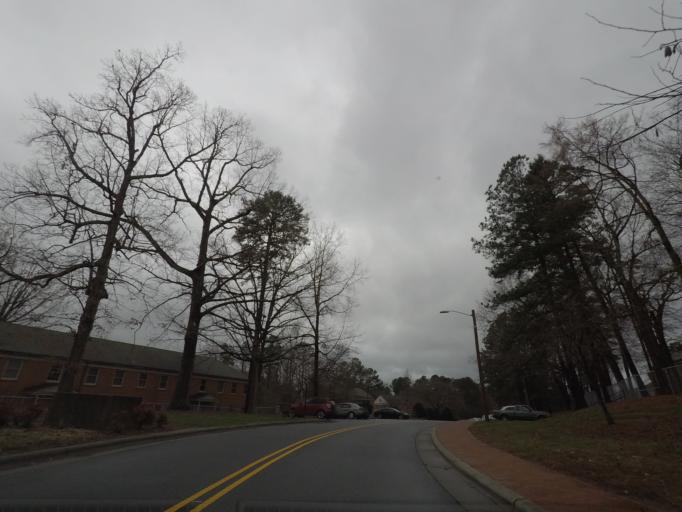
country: US
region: North Carolina
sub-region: Orange County
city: Chapel Hill
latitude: 35.9017
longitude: -79.0489
